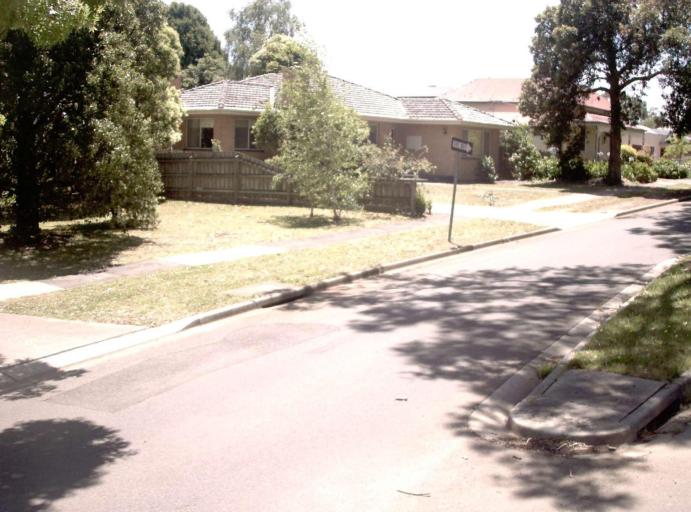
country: AU
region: Victoria
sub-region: Baw Baw
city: Warragul
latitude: -38.0143
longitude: 145.9551
